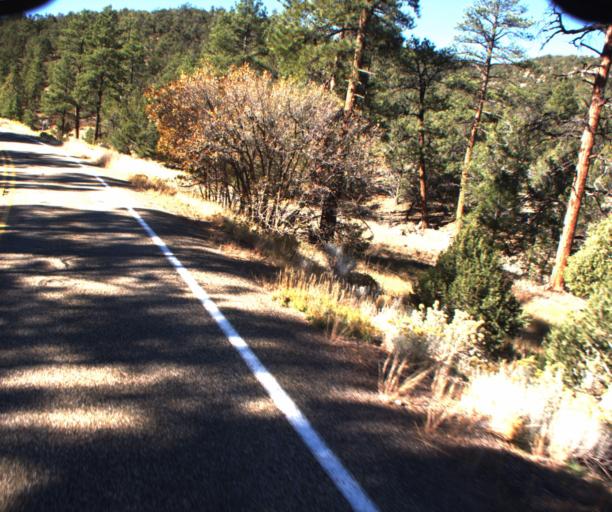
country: US
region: Arizona
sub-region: Coconino County
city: Fredonia
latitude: 36.7380
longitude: -112.1272
